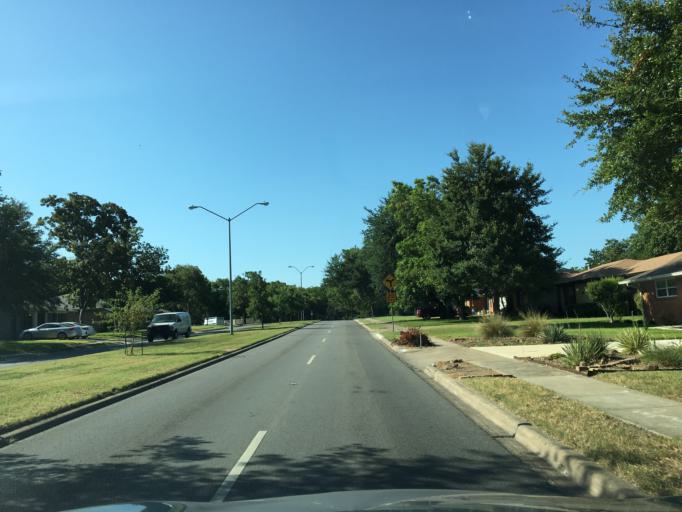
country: US
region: Texas
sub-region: Dallas County
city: Highland Park
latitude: 32.8619
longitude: -96.7103
